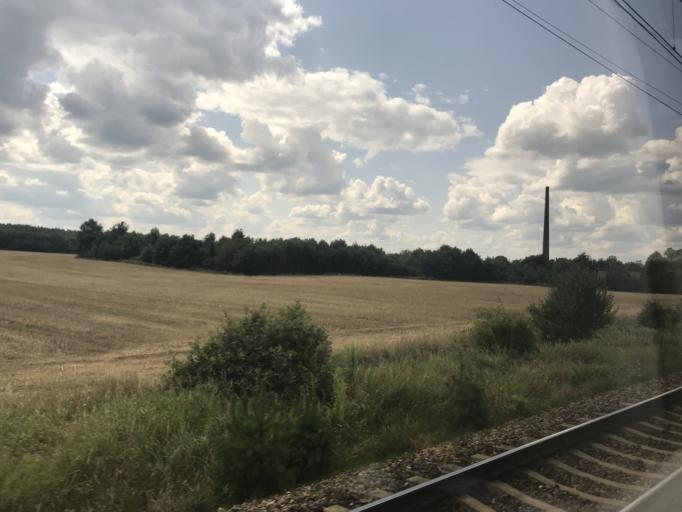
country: PL
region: Lubusz
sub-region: Powiat sulecinski
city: Torzym
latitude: 52.3229
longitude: 15.0053
